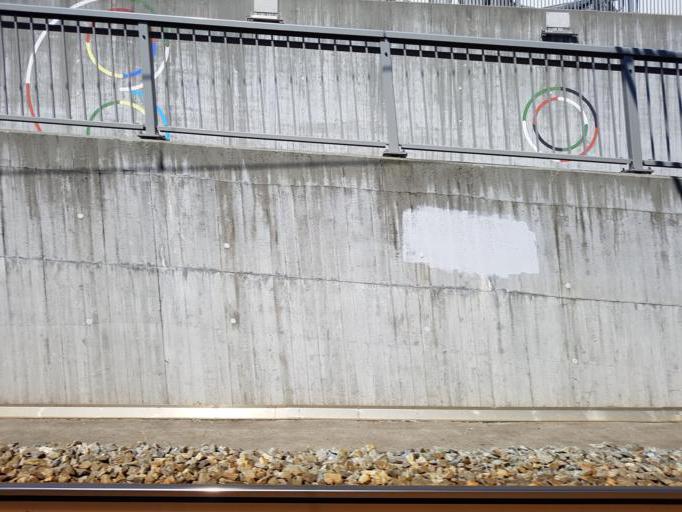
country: NO
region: Hordaland
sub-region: Bergen
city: Ytrebygda
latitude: 60.2968
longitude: 5.2717
